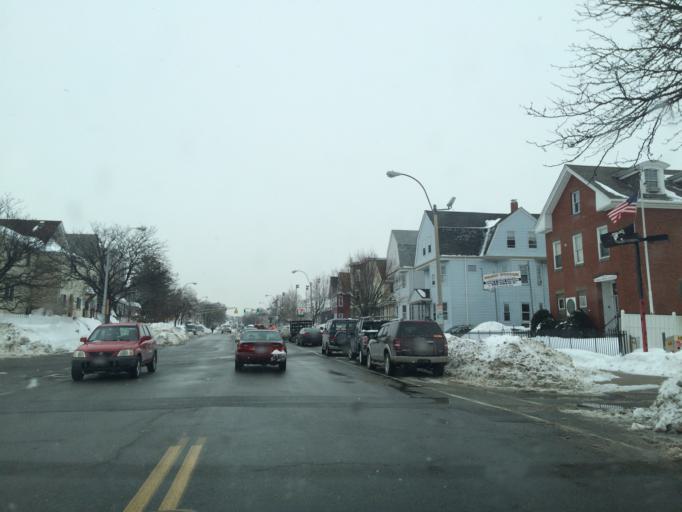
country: US
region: Massachusetts
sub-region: Middlesex County
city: Somerville
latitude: 42.3991
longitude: -71.1097
